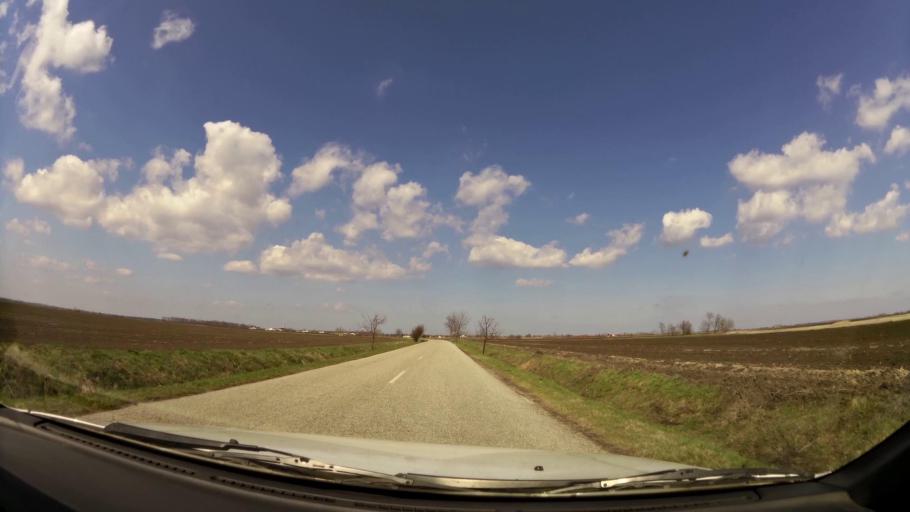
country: HU
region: Pest
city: Tapiogyorgye
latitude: 47.3121
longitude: 19.9439
